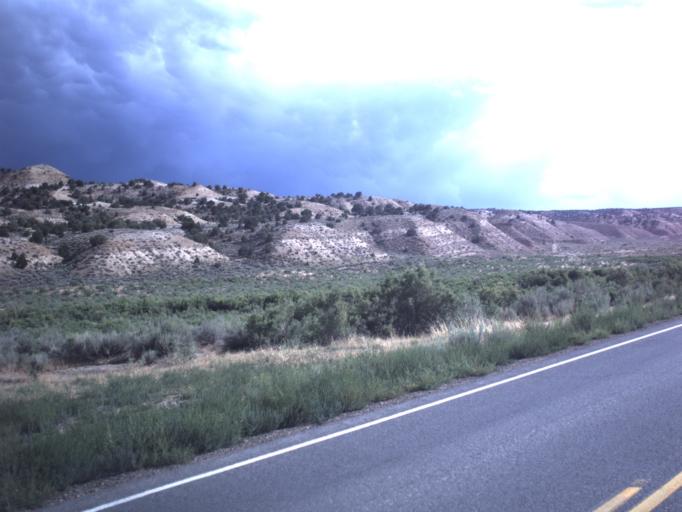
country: US
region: Utah
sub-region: Duchesne County
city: Duchesne
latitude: 40.1454
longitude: -110.4189
